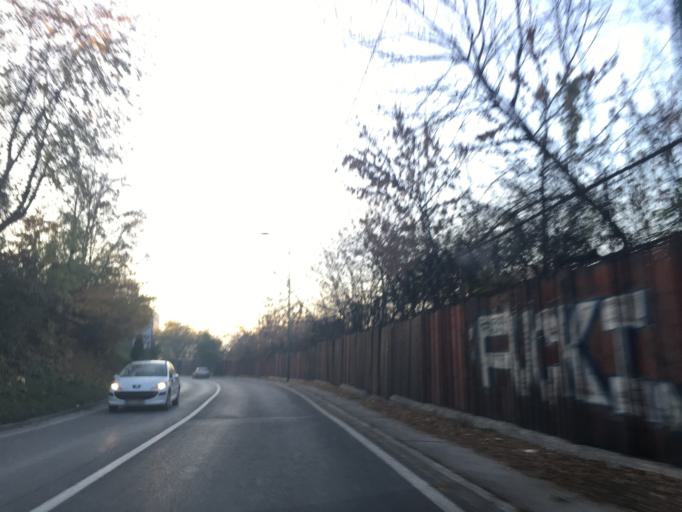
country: BA
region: Federation of Bosnia and Herzegovina
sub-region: Kanton Sarajevo
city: Sarajevo
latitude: 43.8459
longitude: 18.3860
